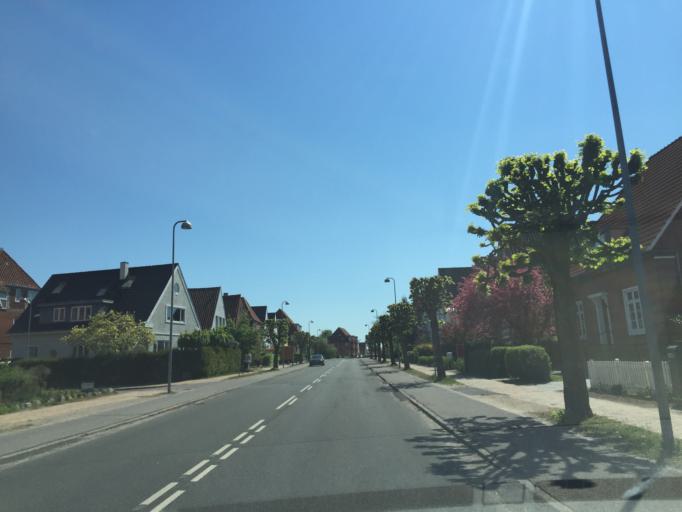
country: DK
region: South Denmark
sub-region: Odense Kommune
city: Odense
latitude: 55.3883
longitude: 10.4008
